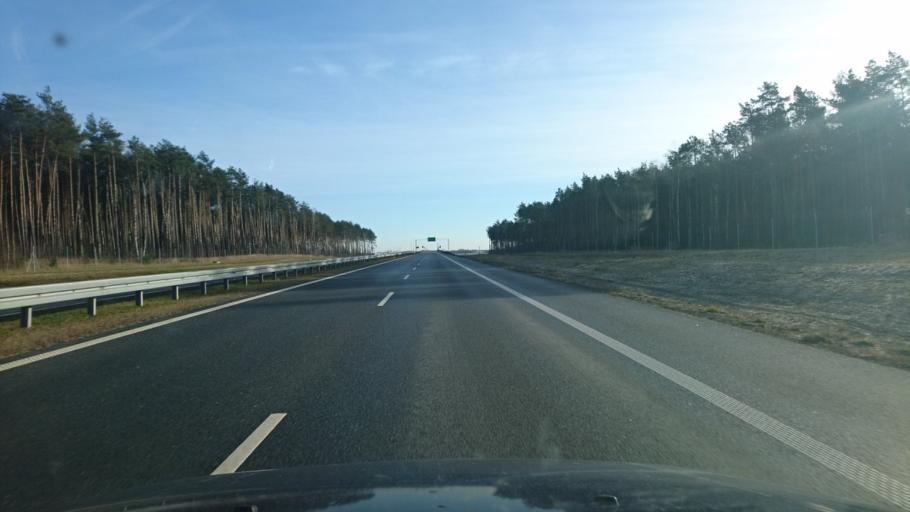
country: PL
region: Greater Poland Voivodeship
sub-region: Powiat kepinski
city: Kepno
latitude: 51.3262
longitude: 17.9894
